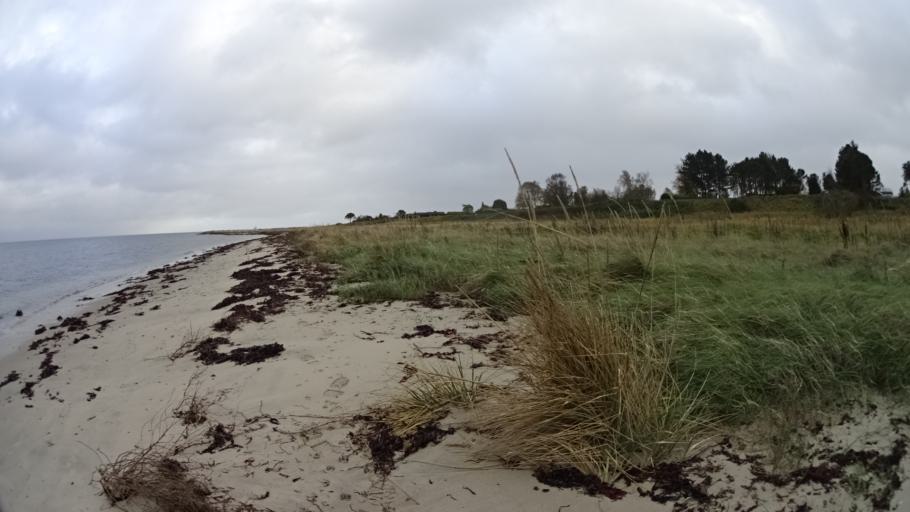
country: DK
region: Central Jutland
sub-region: Arhus Kommune
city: Beder
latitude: 56.0237
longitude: 10.2685
